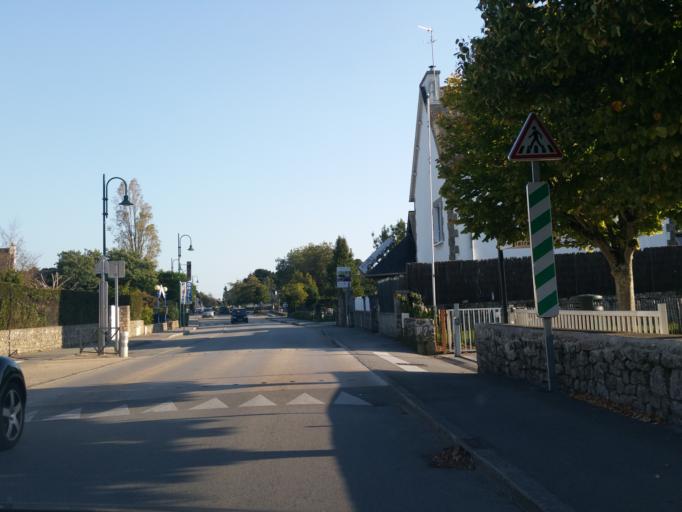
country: FR
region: Brittany
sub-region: Departement du Morbihan
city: Carnac
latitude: 47.5868
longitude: -3.0770
